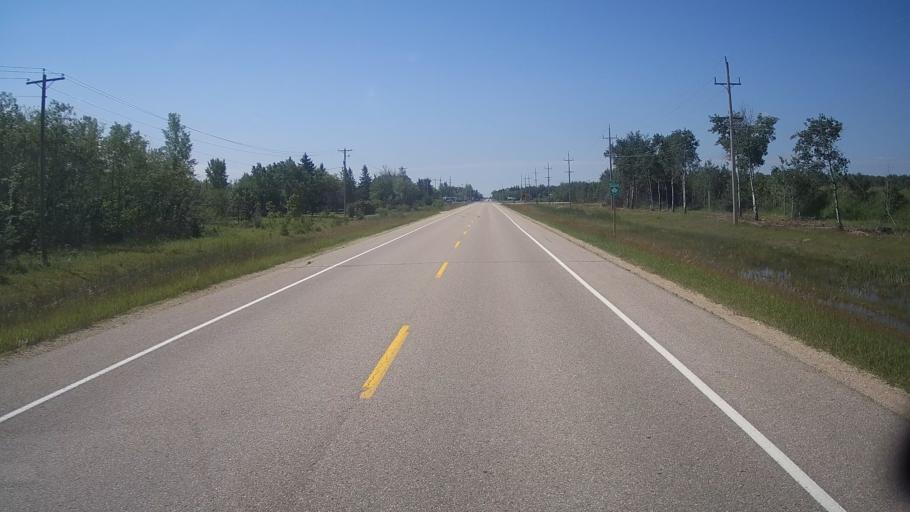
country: CA
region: Manitoba
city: La Broquerie
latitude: 49.6684
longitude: -96.4569
